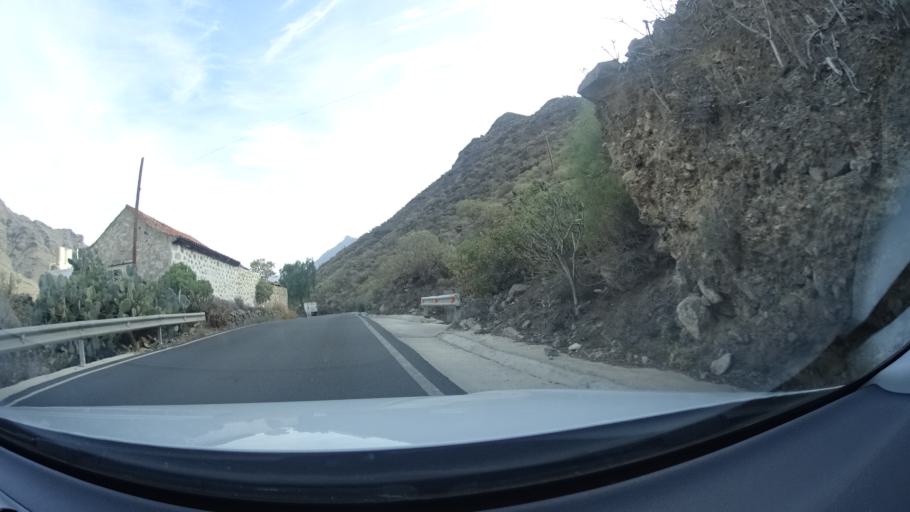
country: ES
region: Canary Islands
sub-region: Provincia de Las Palmas
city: Mogan
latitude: 27.8675
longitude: -15.7401
